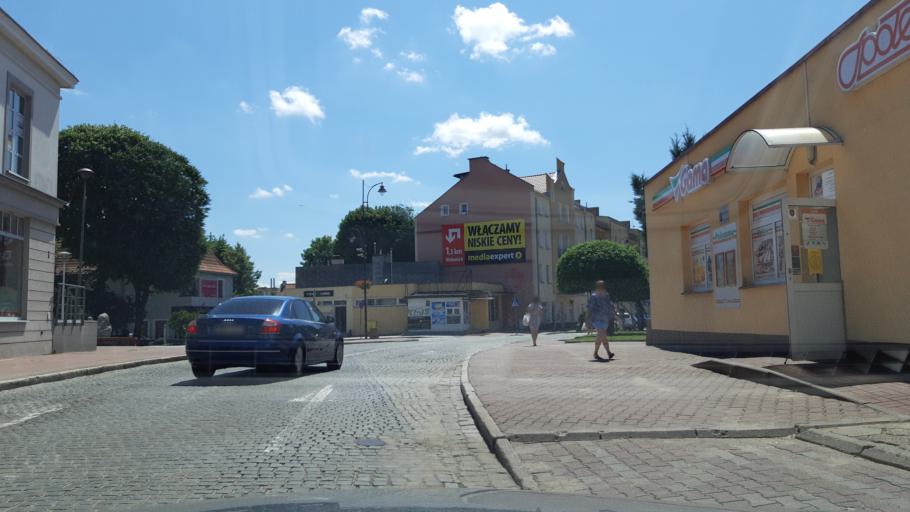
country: PL
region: Warmian-Masurian Voivodeship
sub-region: Powiat mragowski
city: Mragowo
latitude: 53.8674
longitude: 21.3058
